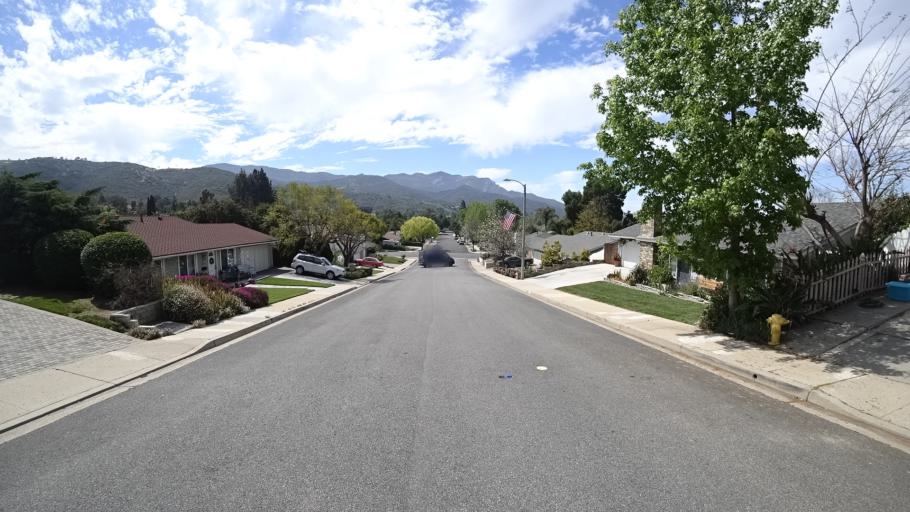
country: US
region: California
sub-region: Ventura County
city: Casa Conejo
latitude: 34.1670
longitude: -118.9396
